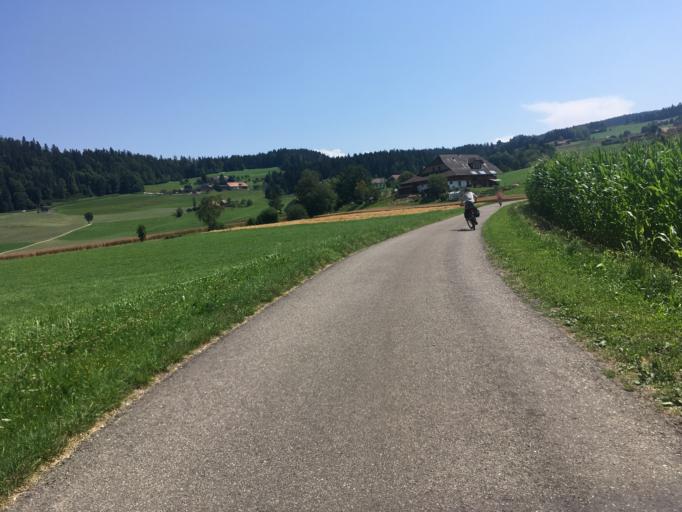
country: CH
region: Bern
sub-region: Bern-Mittelland District
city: Bowil
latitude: 46.8985
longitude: 7.7048
